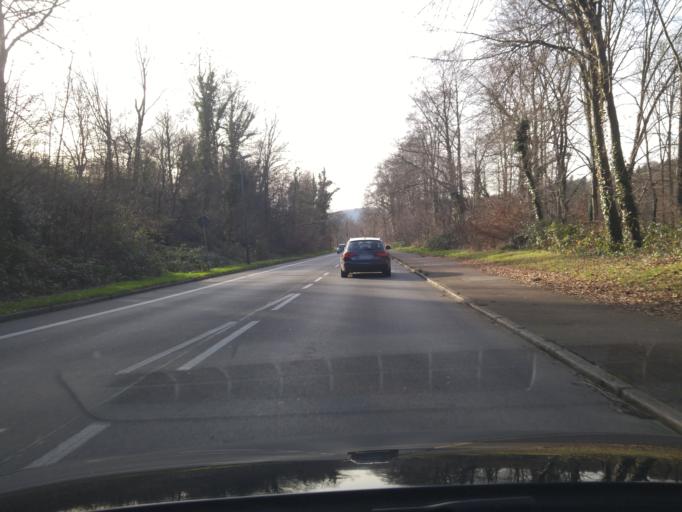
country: DE
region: North Rhine-Westphalia
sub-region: Regierungsbezirk Dusseldorf
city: Essen
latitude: 51.4154
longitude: 7.0214
